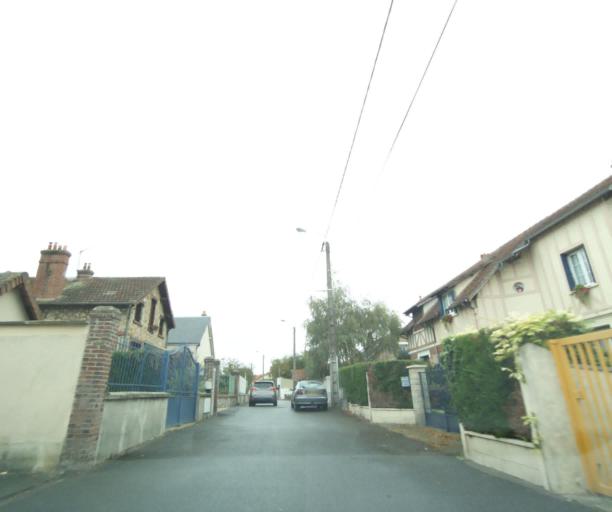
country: FR
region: Centre
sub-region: Departement d'Eure-et-Loir
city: Dreux
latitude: 48.7273
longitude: 1.3645
